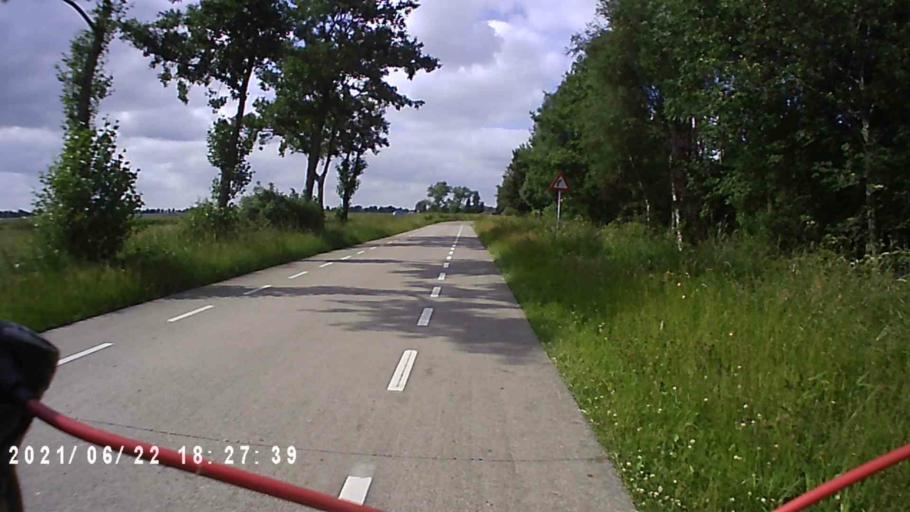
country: NL
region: Groningen
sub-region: Gemeente Zuidhorn
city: Aduard
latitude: 53.1982
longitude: 6.4614
